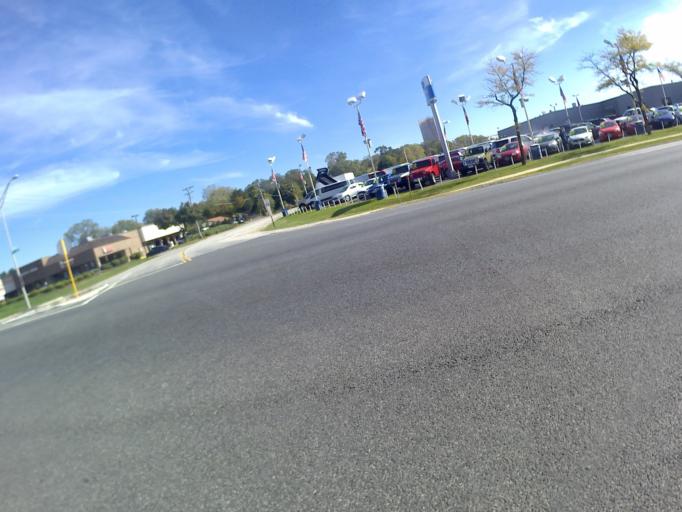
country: US
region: Illinois
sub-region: DuPage County
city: Willowbrook
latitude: 41.7553
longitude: -87.9445
